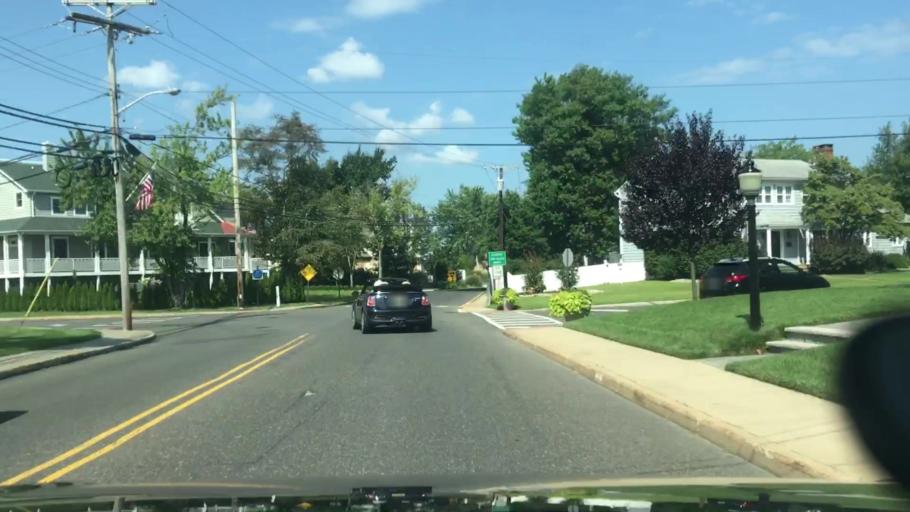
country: US
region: New Jersey
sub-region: Monmouth County
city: Monmouth Beach
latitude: 40.3321
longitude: -73.9879
